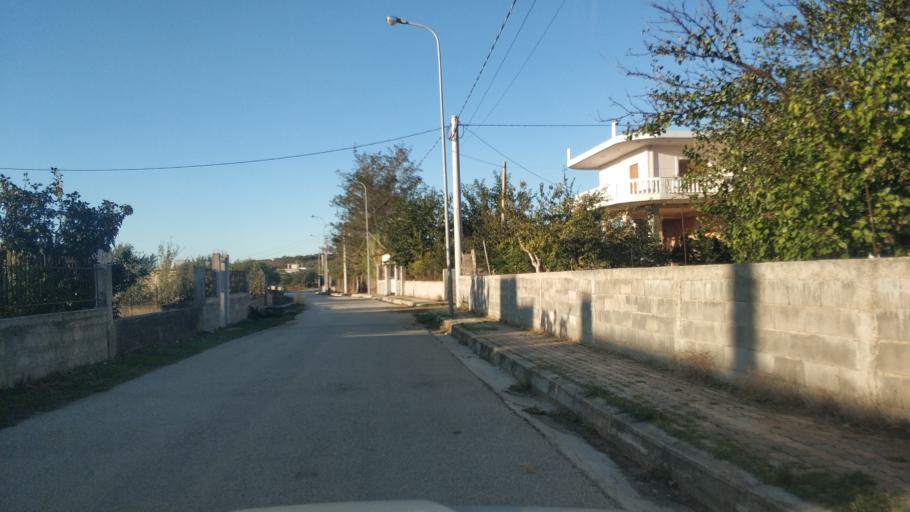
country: AL
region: Vlore
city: Vlore
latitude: 40.5091
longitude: 19.4104
